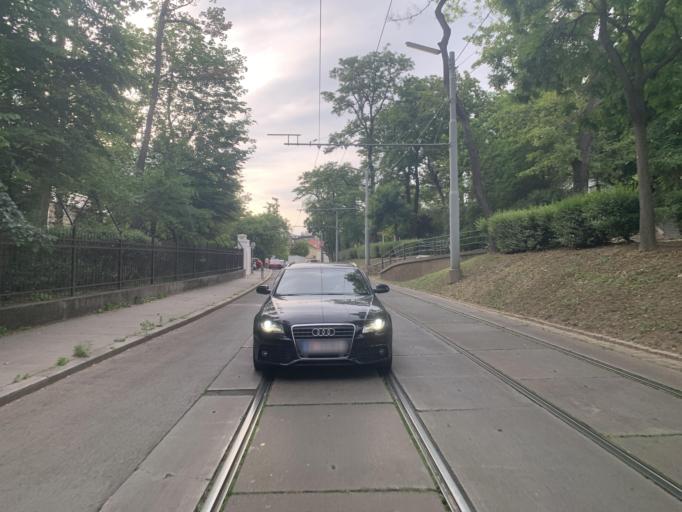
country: AT
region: Vienna
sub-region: Wien Stadt
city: Vienna
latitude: 48.2468
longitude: 16.3559
